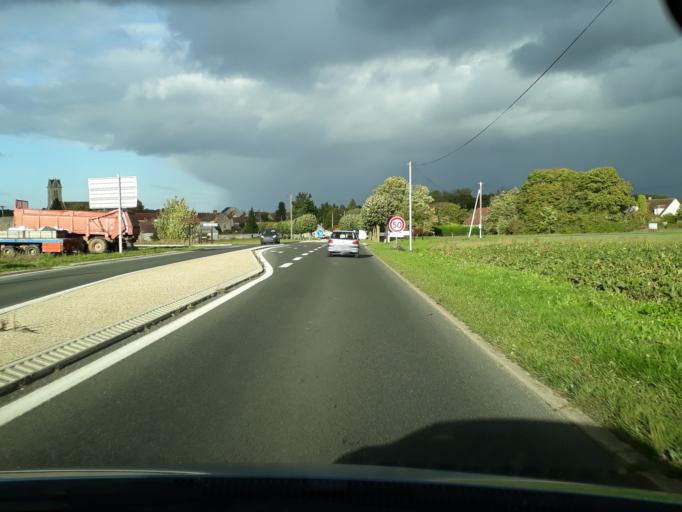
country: FR
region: Ile-de-France
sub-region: Departement de Seine-et-Marne
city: Acheres-la-Foret
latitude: 48.3394
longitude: 2.5990
